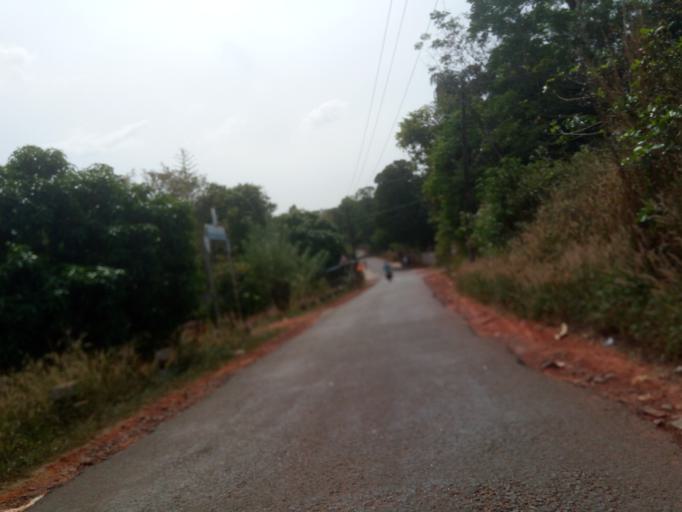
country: IN
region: Kerala
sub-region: Malappuram
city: Ponnani
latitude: 10.7970
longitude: 76.0327
